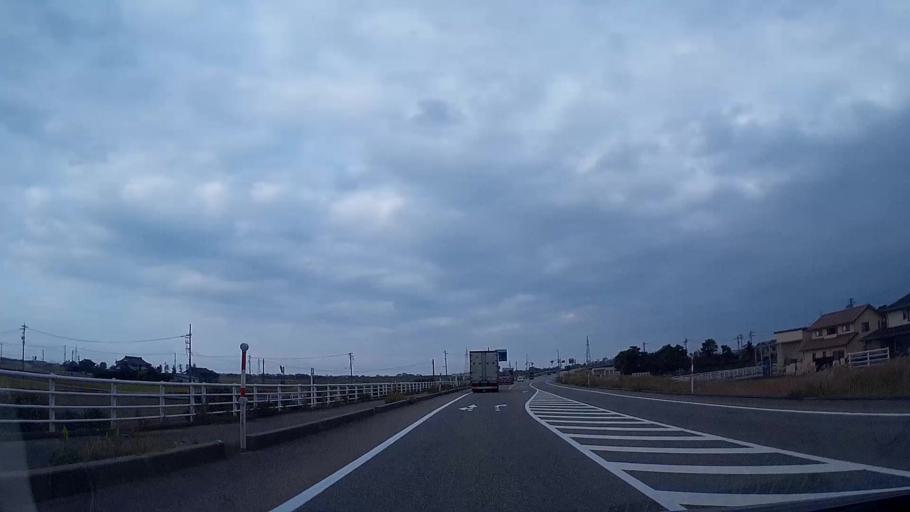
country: JP
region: Toyama
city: Nyuzen
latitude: 36.8974
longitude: 137.4449
